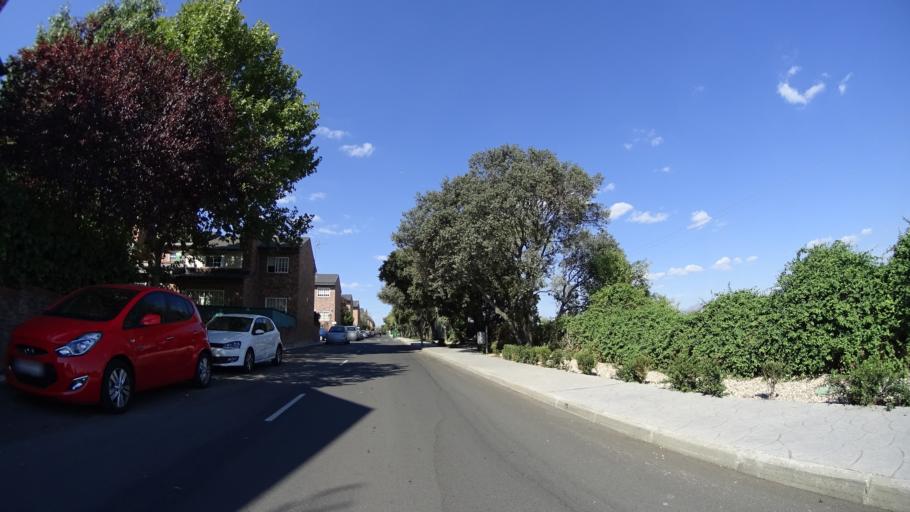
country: ES
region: Madrid
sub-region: Provincia de Madrid
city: Navalquejigo
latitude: 40.6083
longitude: -4.0259
